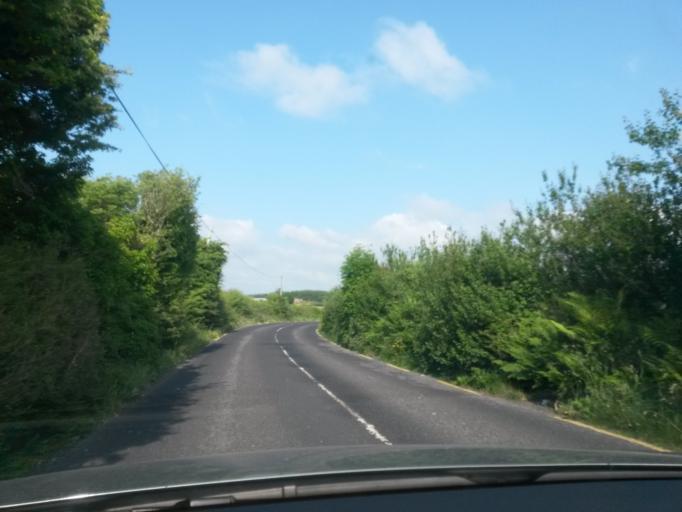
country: IE
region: Munster
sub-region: An Clar
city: Ennis
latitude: 52.8727
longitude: -9.2493
